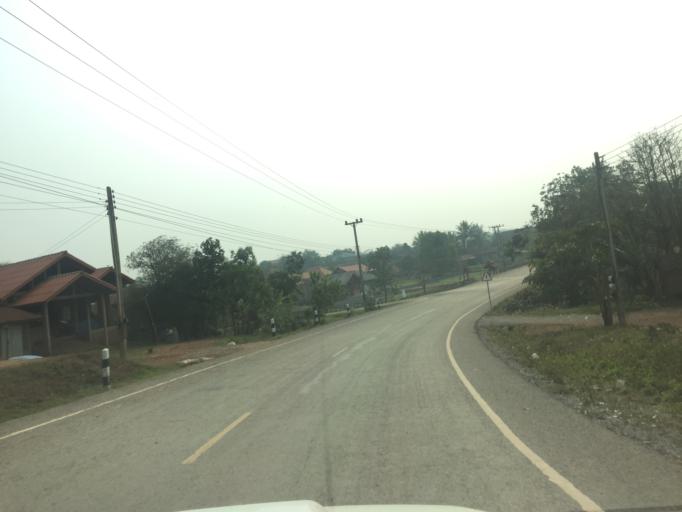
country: TH
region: Nan
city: Song Khwae
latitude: 19.5825
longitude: 100.7497
